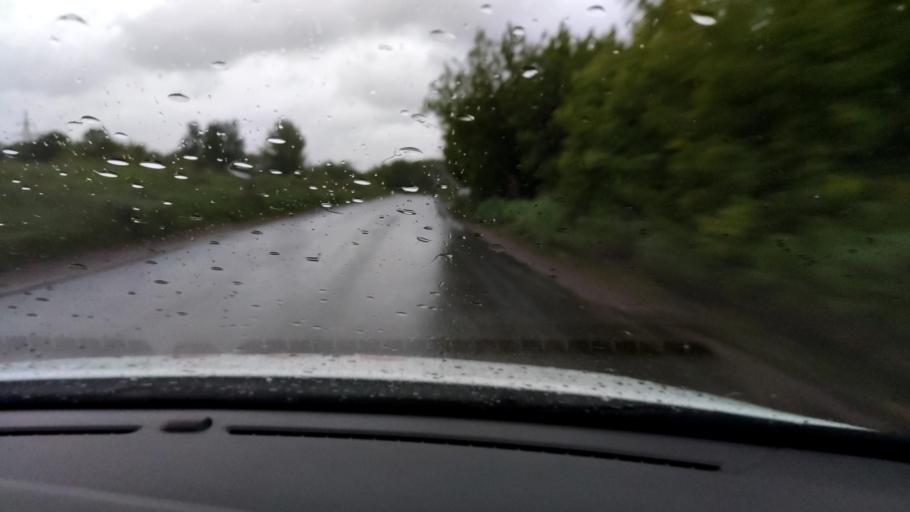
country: RU
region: Tatarstan
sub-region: Gorod Kazan'
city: Kazan
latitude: 55.7222
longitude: 49.1162
